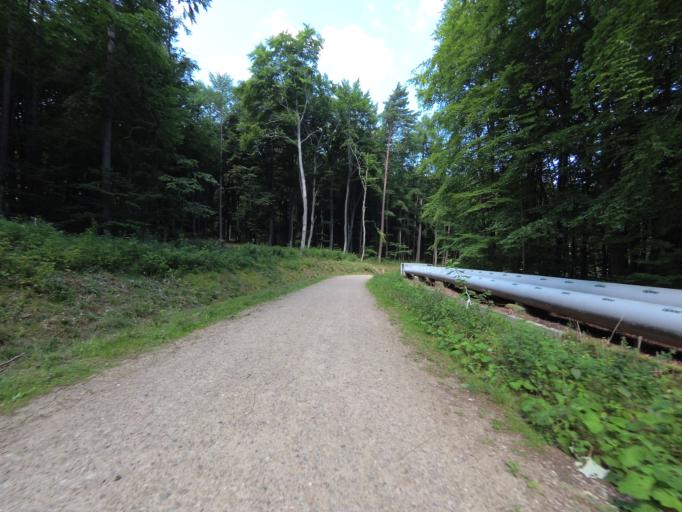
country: PL
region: Pomeranian Voivodeship
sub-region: Gdynia
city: Wielki Kack
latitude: 54.4789
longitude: 18.5010
